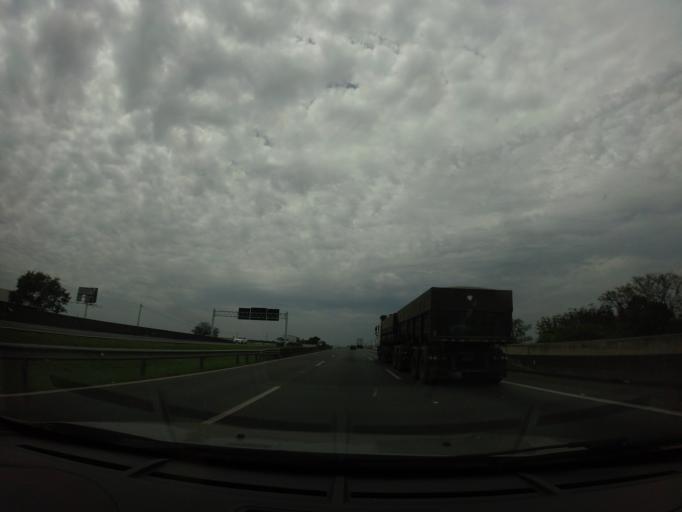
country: BR
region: Sao Paulo
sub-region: Sumare
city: Sumare
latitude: -22.7917
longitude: -47.2267
